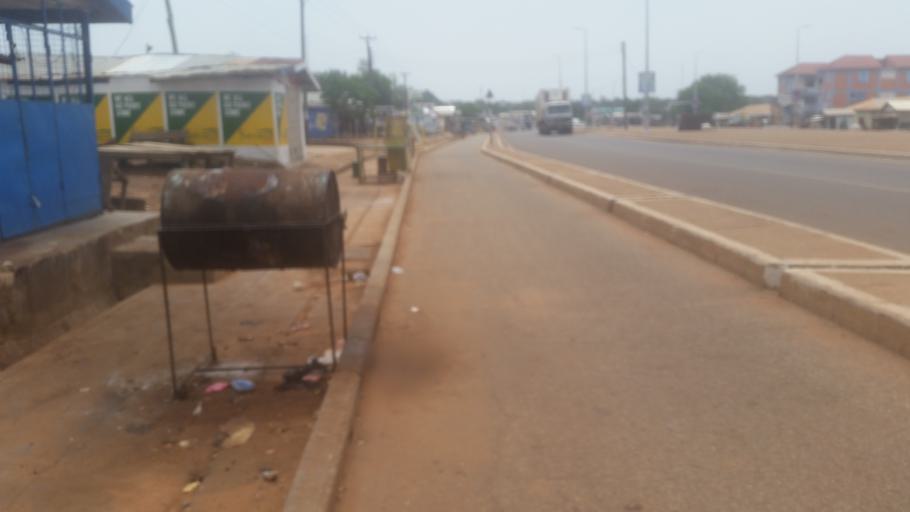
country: GH
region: Northern
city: Tamale
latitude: 9.3949
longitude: -0.8245
